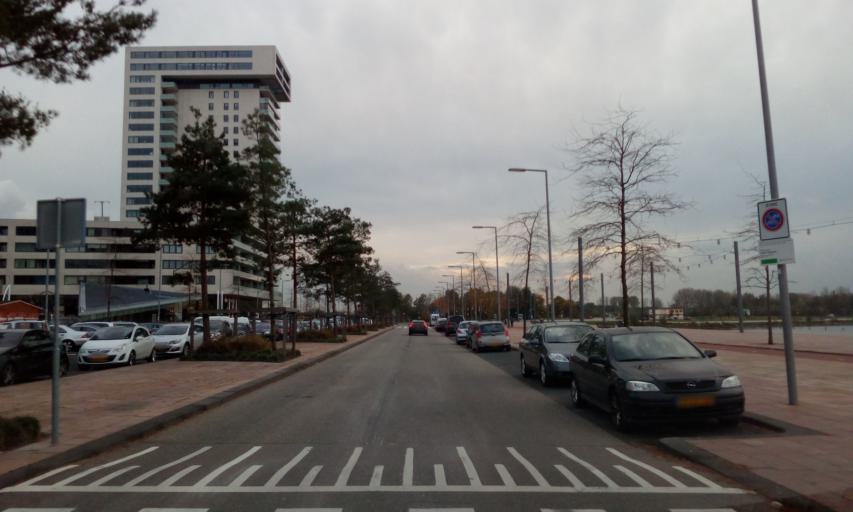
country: NL
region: South Holland
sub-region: Gemeente Capelle aan den IJssel
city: Capelle aan den IJssel
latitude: 51.9816
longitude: 4.5813
